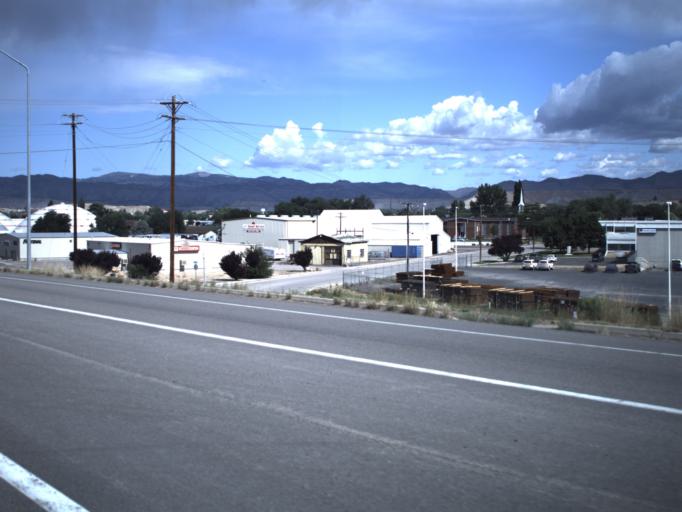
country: US
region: Utah
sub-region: Carbon County
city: Price
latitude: 39.5893
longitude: -110.8152
